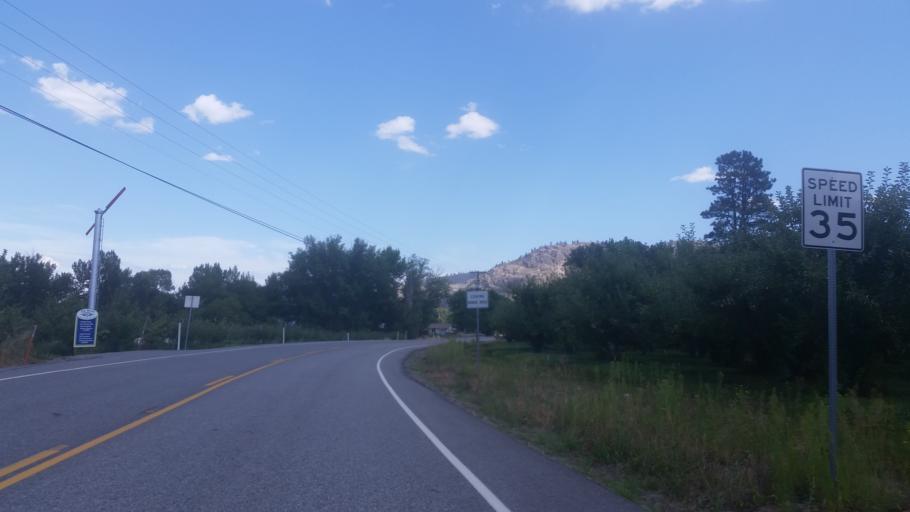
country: US
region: Washington
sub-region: Okanogan County
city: Okanogan
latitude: 48.2828
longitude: -119.7106
